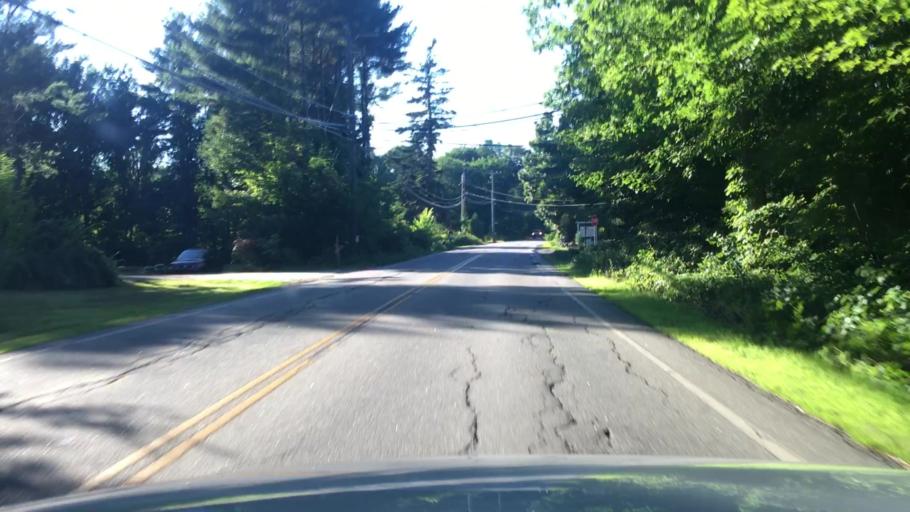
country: US
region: New Hampshire
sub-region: Rockingham County
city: Sandown
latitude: 42.9099
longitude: -71.1600
